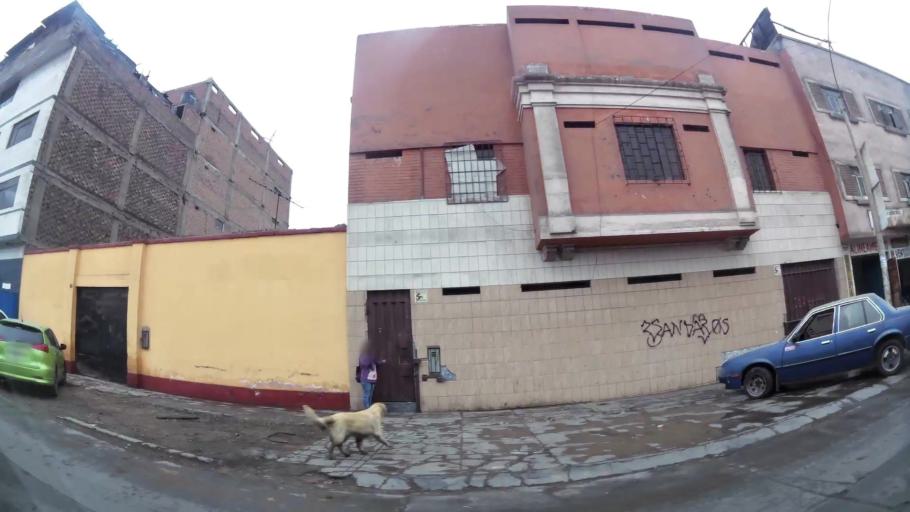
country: PE
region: Lima
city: Lima
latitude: -12.0676
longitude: -77.0257
